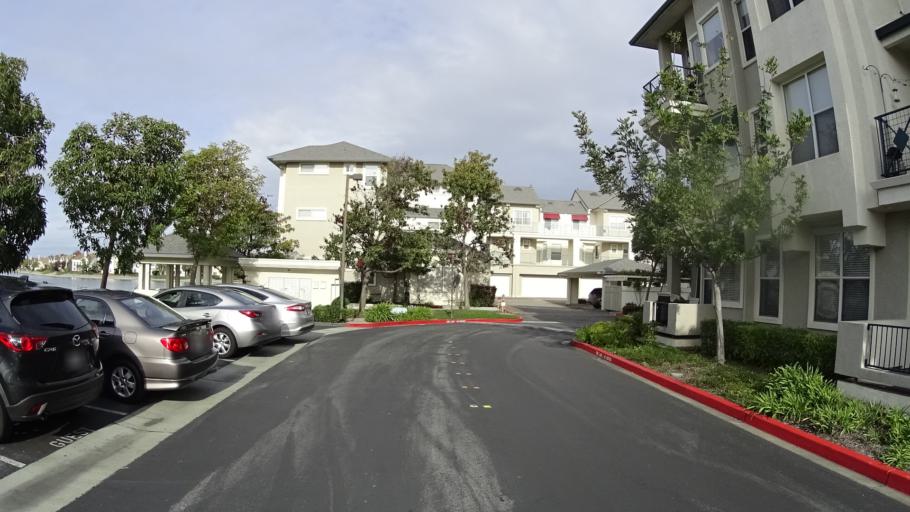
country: US
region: California
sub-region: San Mateo County
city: Redwood Shores
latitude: 37.5401
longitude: -122.2421
